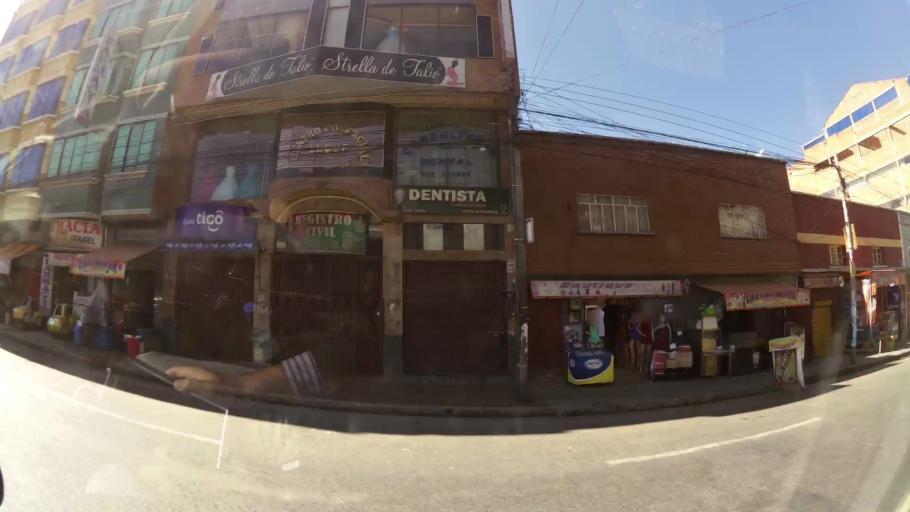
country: BO
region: La Paz
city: La Paz
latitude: -16.4971
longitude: -68.1741
